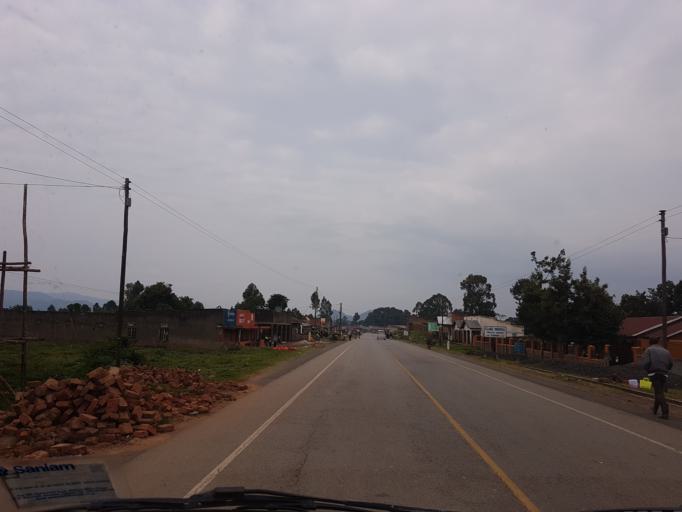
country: UG
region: Western Region
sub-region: Kisoro District
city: Kisoro
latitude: -1.3352
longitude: 29.7371
